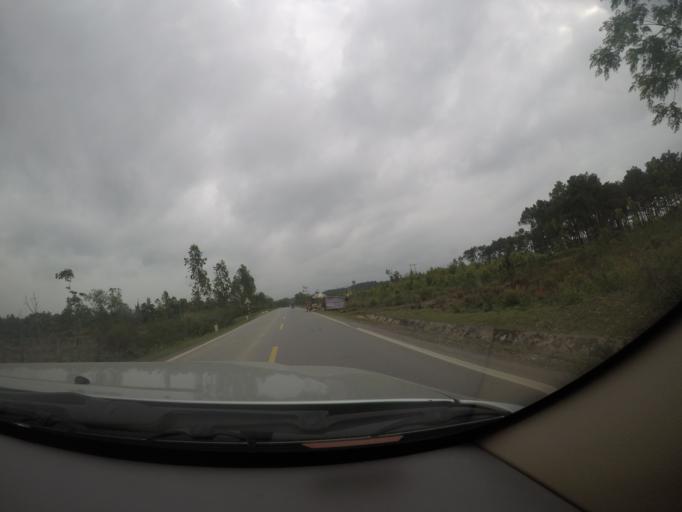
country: VN
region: Quang Binh
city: Quan Hau
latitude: 17.3637
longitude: 106.6226
